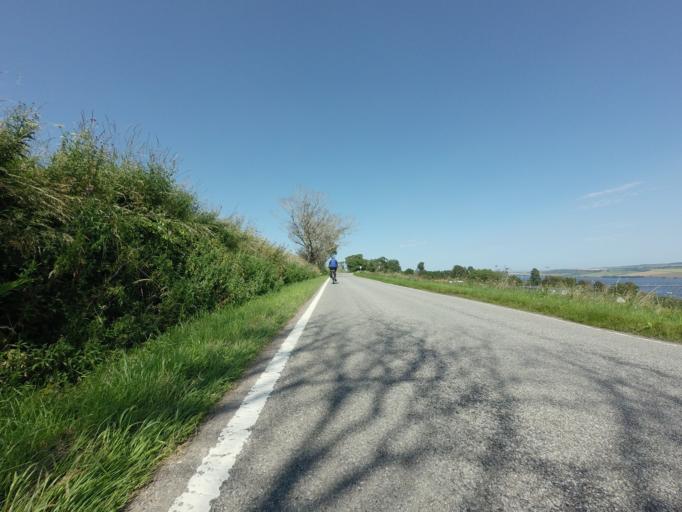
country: GB
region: Scotland
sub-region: Highland
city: Dingwall
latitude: 57.6189
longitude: -4.4030
